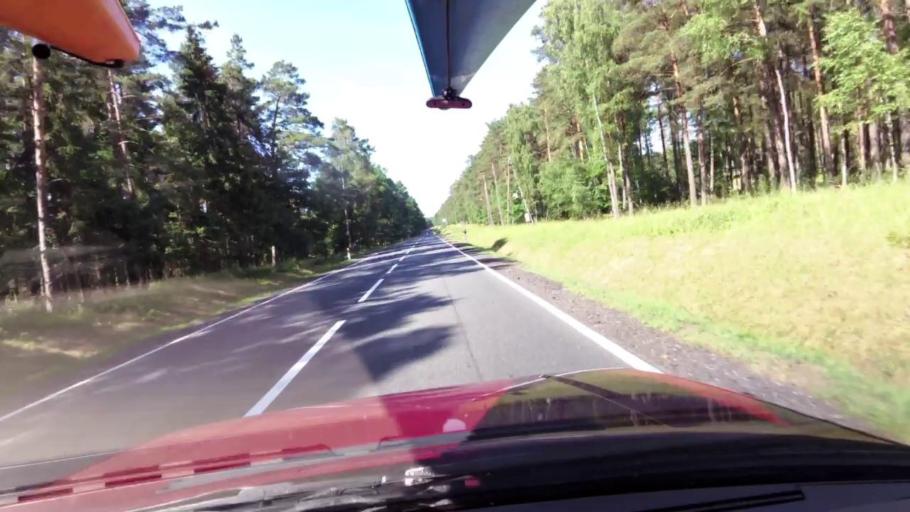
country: PL
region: Pomeranian Voivodeship
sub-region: Powiat bytowski
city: Miastko
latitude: 54.1184
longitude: 17.0017
